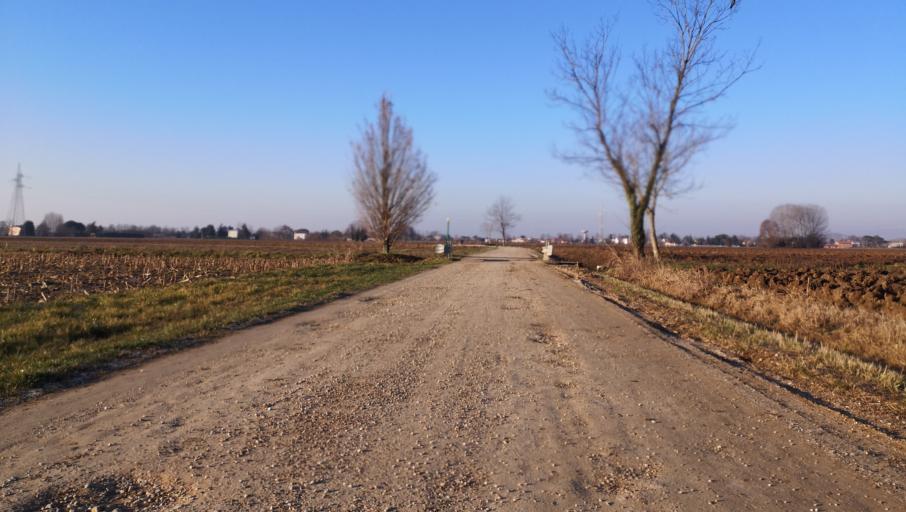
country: IT
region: Friuli Venezia Giulia
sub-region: Provincia di Udine
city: Pavia di Udine
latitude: 45.9821
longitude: 13.2959
